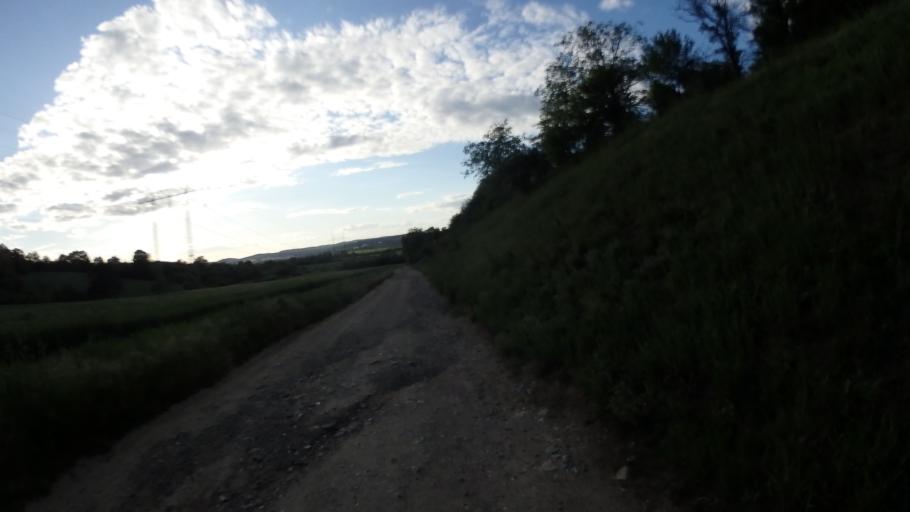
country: CZ
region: South Moravian
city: Ostopovice
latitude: 49.1583
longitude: 16.5403
